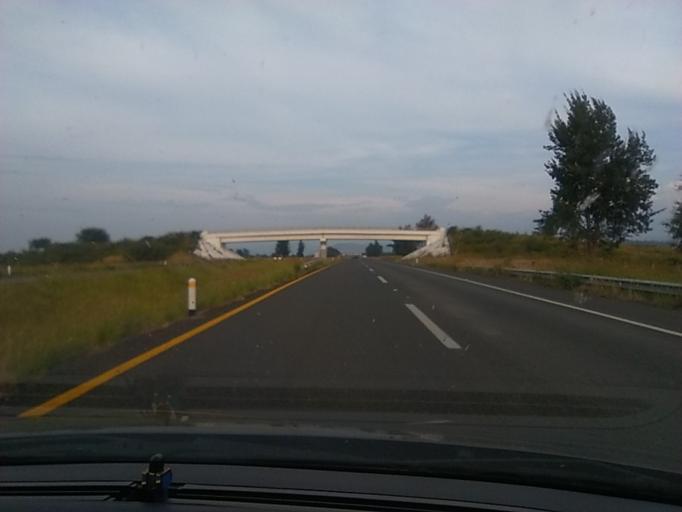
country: MX
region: Michoacan
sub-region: Alvaro Obregon
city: Tzintzimeo
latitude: 19.8914
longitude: -100.9986
